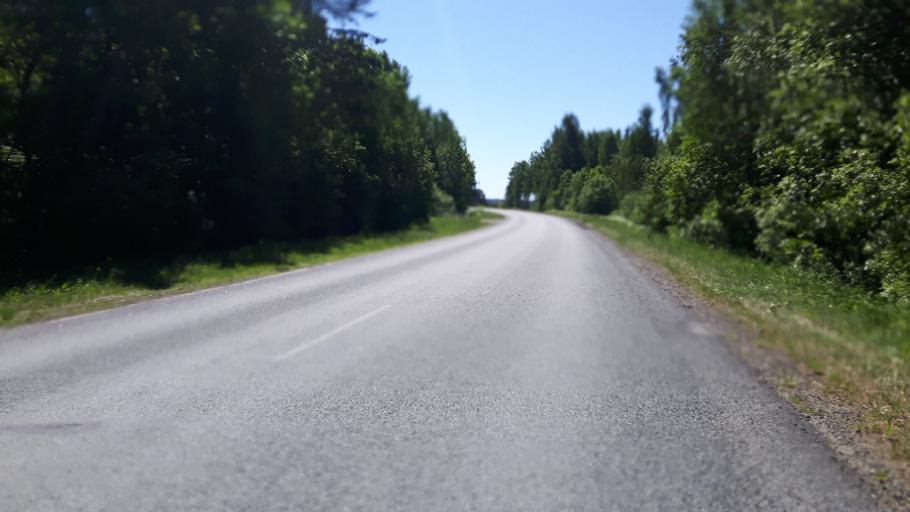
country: EE
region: Harju
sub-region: Kuusalu vald
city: Kuusalu
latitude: 59.4728
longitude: 25.4529
